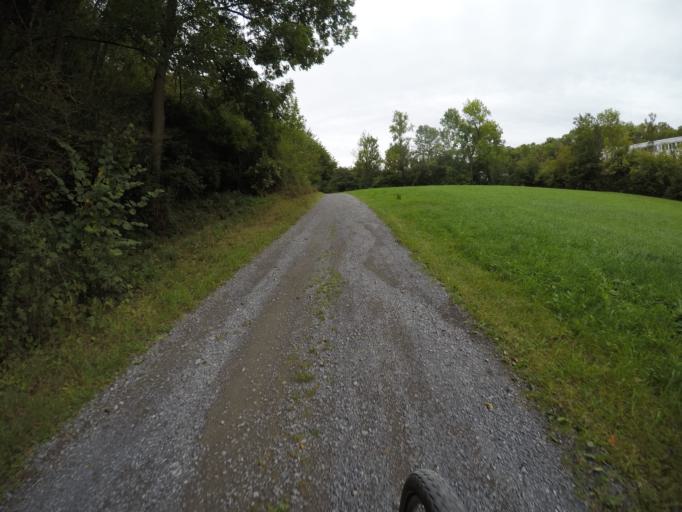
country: DE
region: Baden-Wuerttemberg
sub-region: Regierungsbezirk Stuttgart
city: Eberdingen
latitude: 48.9043
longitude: 8.9795
